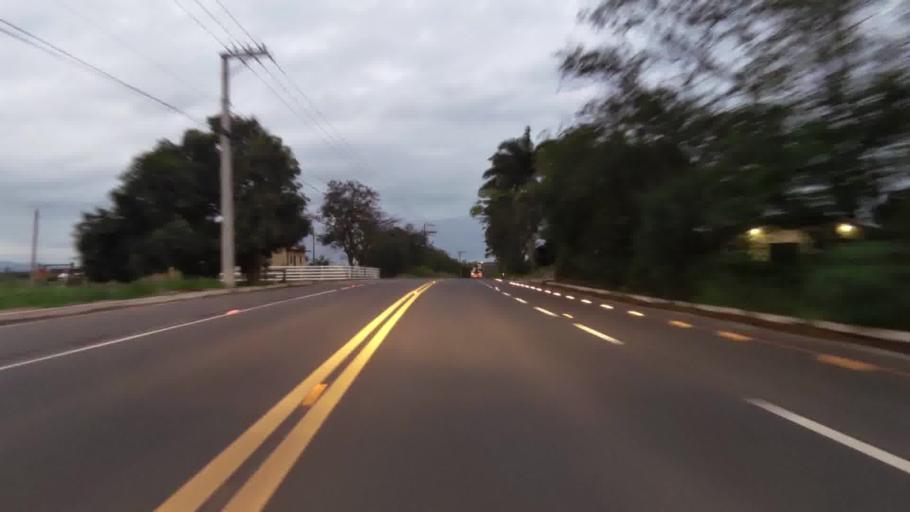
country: BR
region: Espirito Santo
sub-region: Piuma
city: Piuma
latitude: -20.8055
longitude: -40.6090
